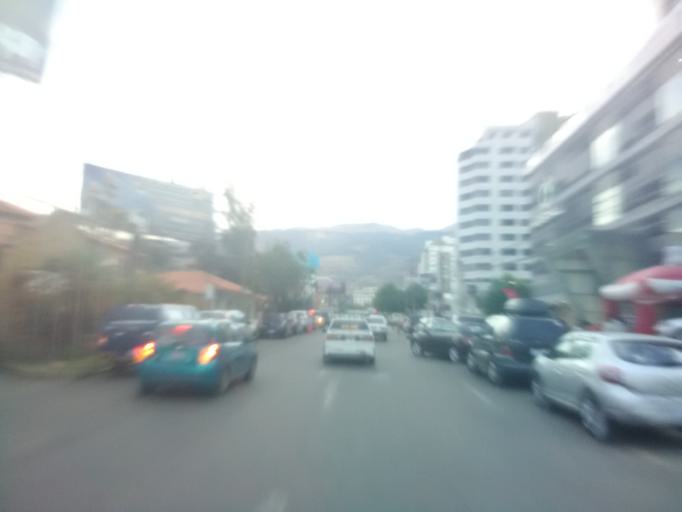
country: BO
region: Cochabamba
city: Cochabamba
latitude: -17.3759
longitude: -66.1511
